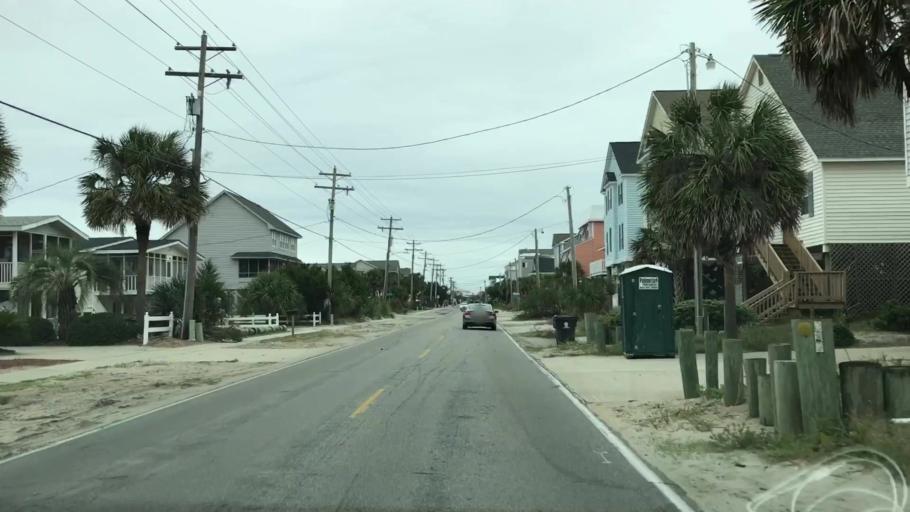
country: US
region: South Carolina
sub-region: Horry County
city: Garden City
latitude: 33.5740
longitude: -79.0012
